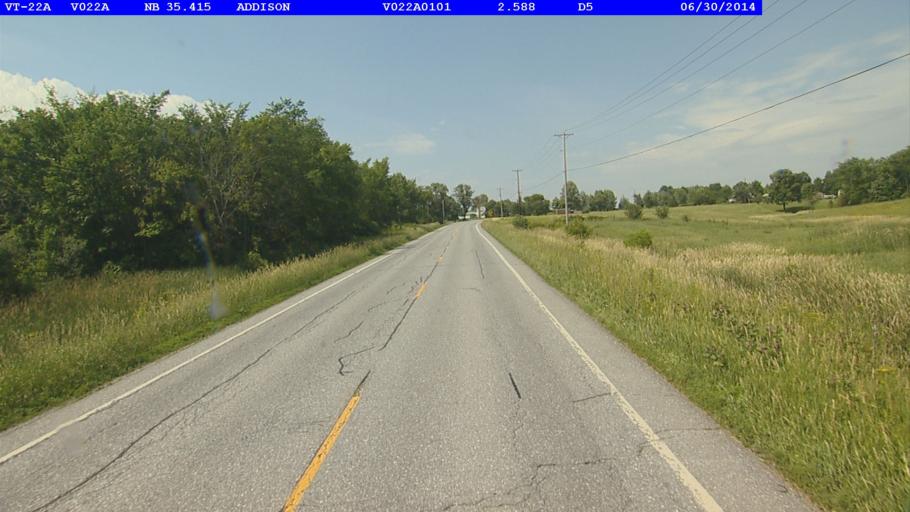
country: US
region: Vermont
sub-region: Addison County
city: Vergennes
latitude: 44.0668
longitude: -73.3040
